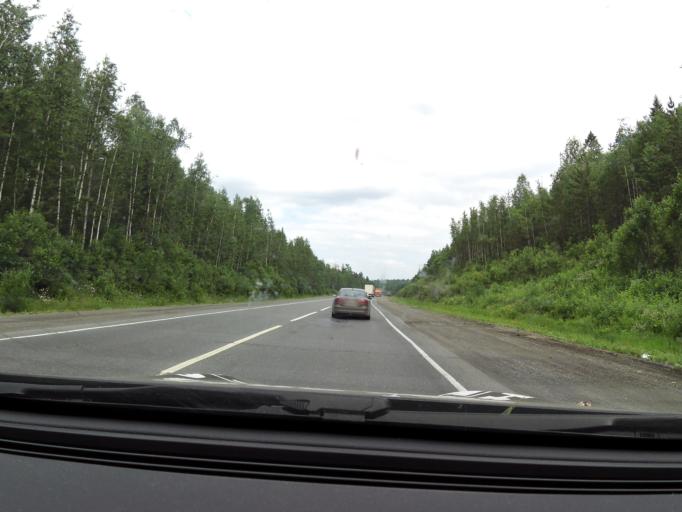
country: RU
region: Sverdlovsk
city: Bilimbay
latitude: 56.8596
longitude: 59.7273
